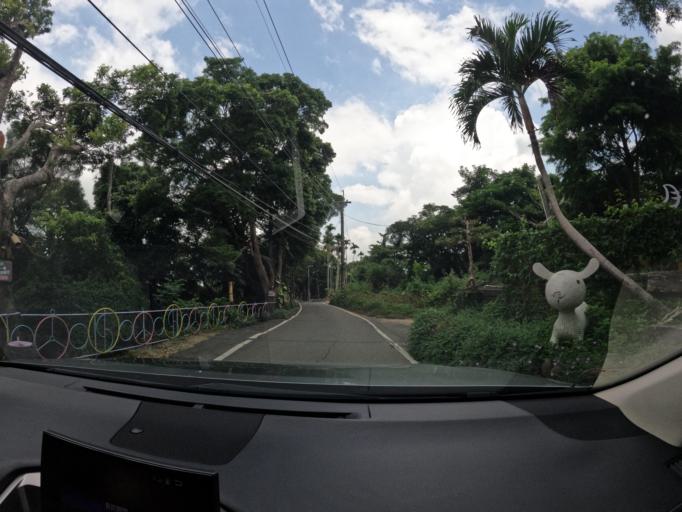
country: TW
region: Taiwan
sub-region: Nantou
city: Nantou
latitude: 23.9098
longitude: 120.6327
